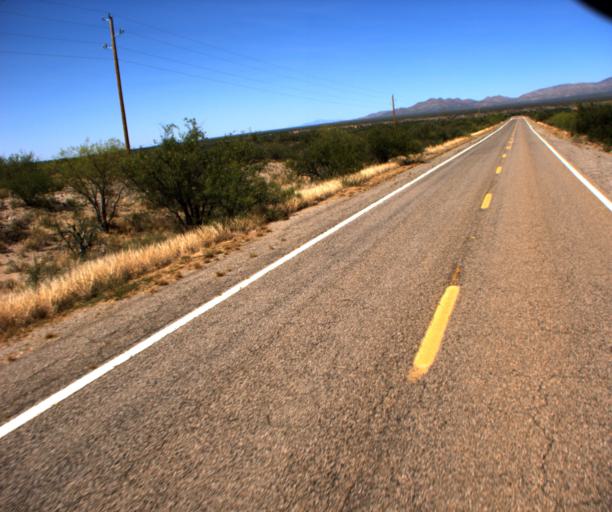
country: US
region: Arizona
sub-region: Pima County
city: Three Points
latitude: 31.8368
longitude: -111.4084
